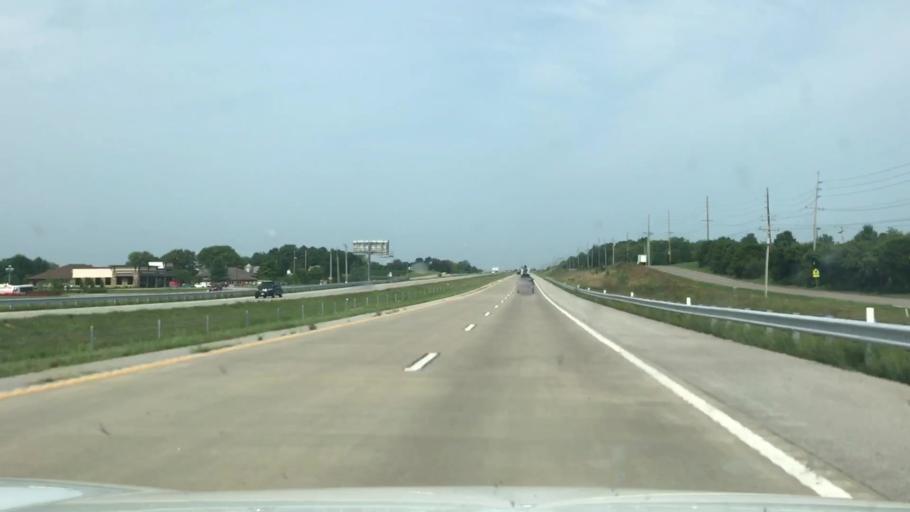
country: US
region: Missouri
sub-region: Saint Charles County
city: Dardenne Prairie
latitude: 38.7605
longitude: -90.7172
